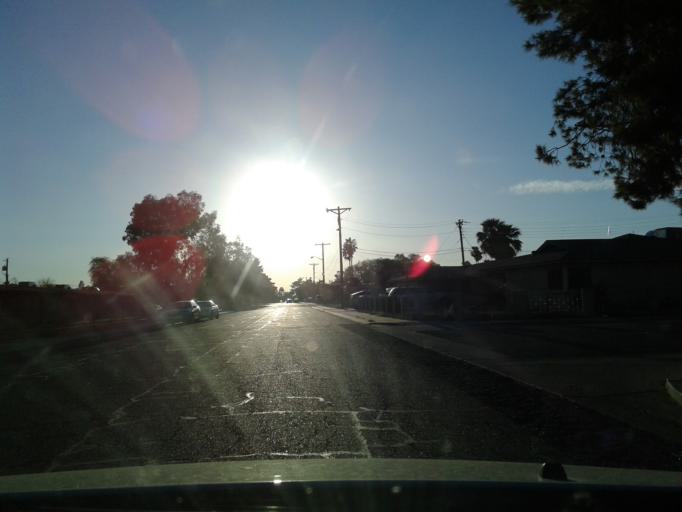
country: US
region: Arizona
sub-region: Maricopa County
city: Phoenix
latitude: 33.5005
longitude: -112.1029
